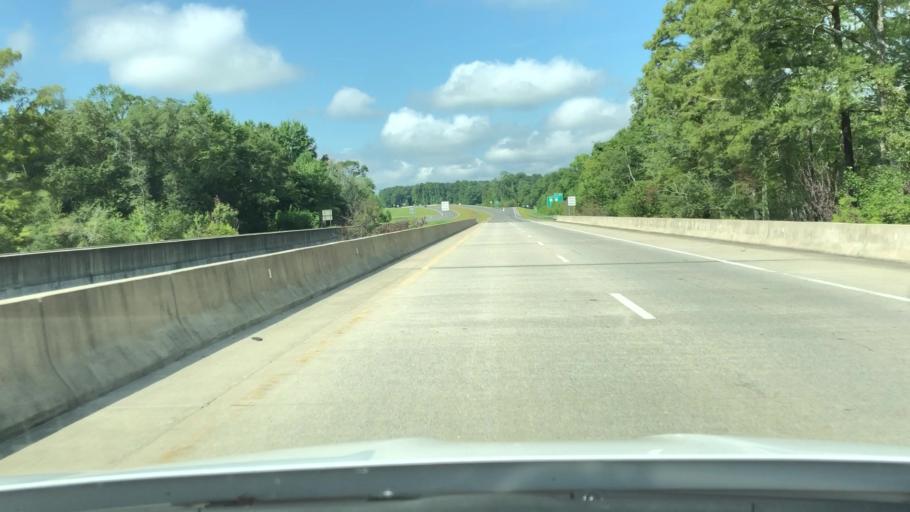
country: US
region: North Carolina
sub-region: Bertie County
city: Windsor
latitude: 36.0140
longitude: -76.9462
